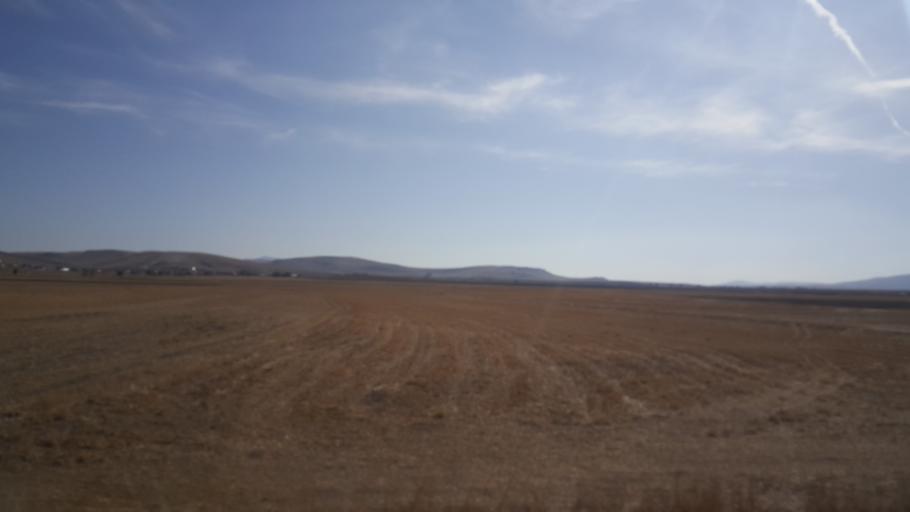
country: TR
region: Ankara
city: Yenice
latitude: 39.3820
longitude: 32.8016
